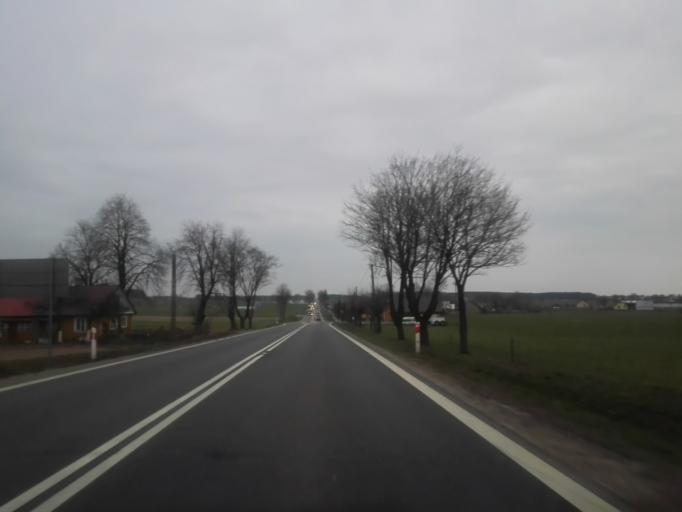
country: PL
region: Podlasie
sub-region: Powiat kolnenski
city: Stawiski
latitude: 53.4662
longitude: 22.2011
